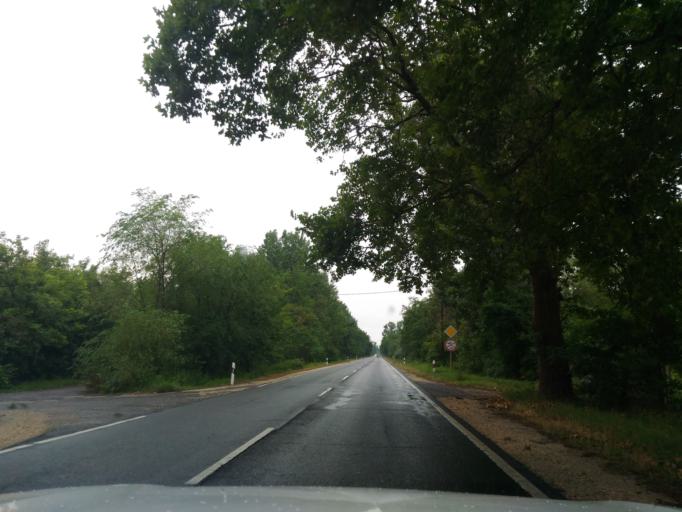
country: HU
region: Pest
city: Ocsa
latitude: 47.2658
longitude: 19.2143
